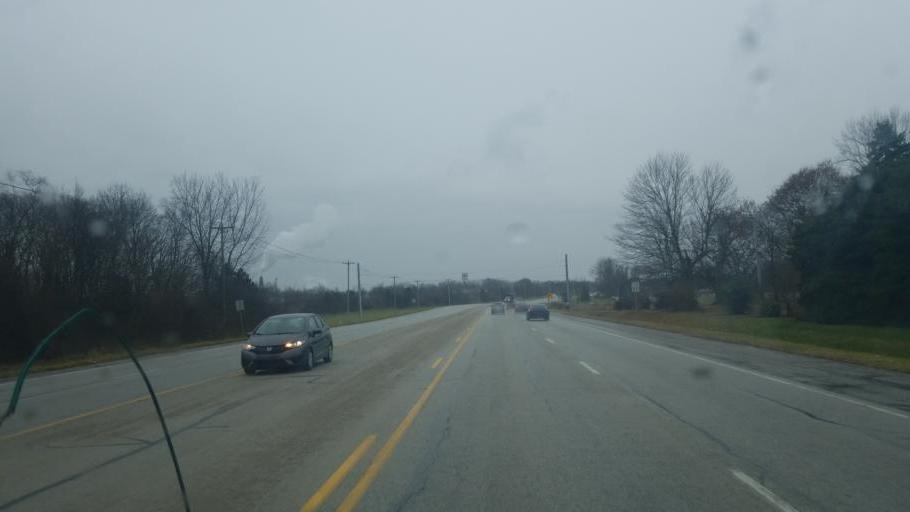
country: US
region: Indiana
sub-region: Shelby County
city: Shelbyville
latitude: 39.5424
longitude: -85.7754
